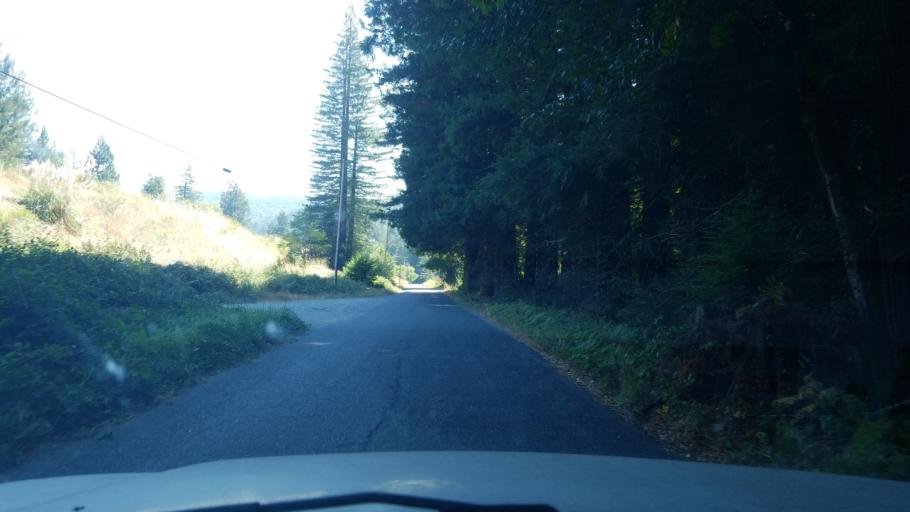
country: US
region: California
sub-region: Humboldt County
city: Rio Dell
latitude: 40.3484
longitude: -123.9185
